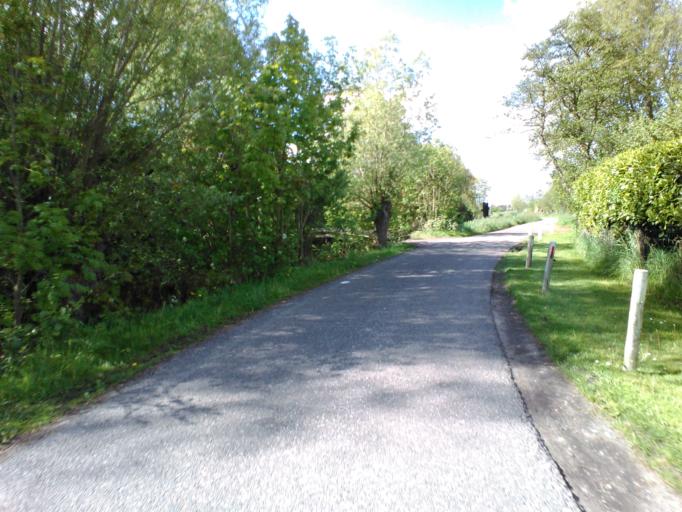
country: NL
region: South Holland
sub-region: Bodegraven-Reeuwijk
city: Reeuwijk
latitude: 52.0391
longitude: 4.7585
